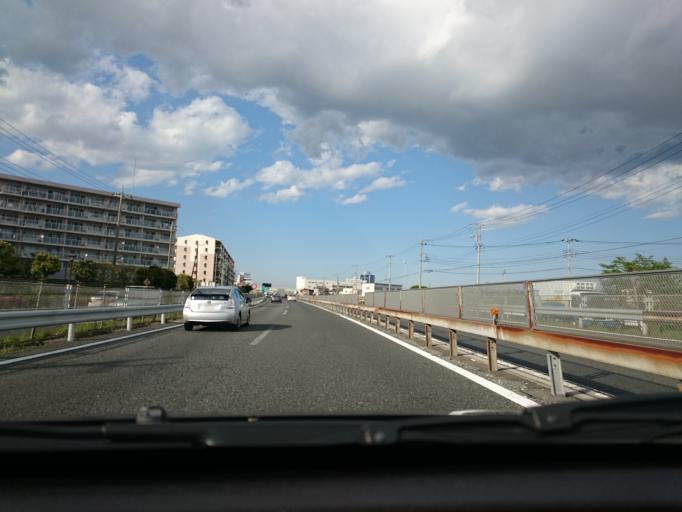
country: JP
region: Kanagawa
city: Atsugi
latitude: 35.4107
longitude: 139.3462
